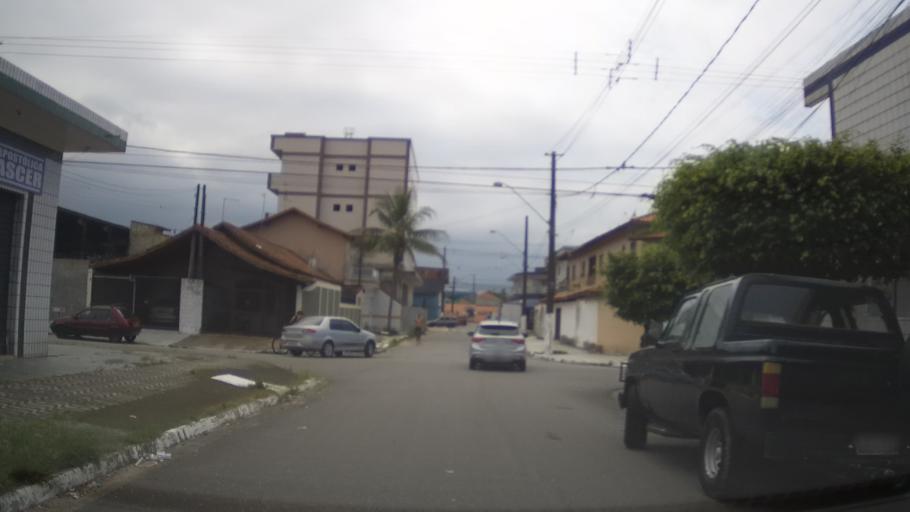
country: BR
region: Sao Paulo
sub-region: Praia Grande
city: Praia Grande
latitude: -24.0244
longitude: -46.4967
